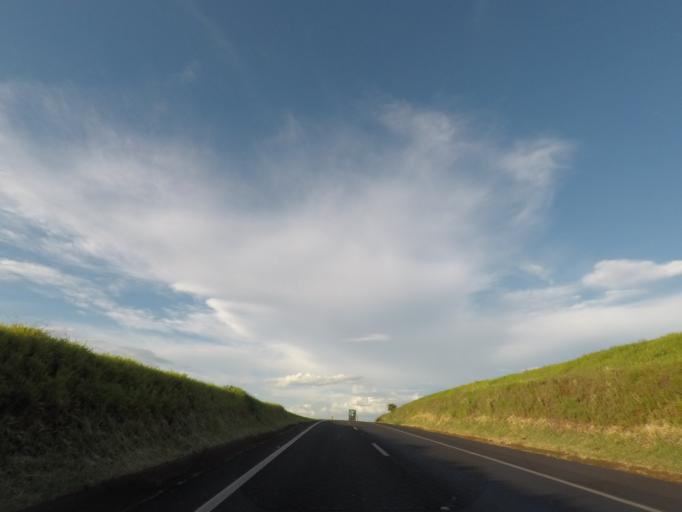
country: BR
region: Sao Paulo
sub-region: Ituverava
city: Ituverava
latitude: -20.2474
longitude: -47.7984
